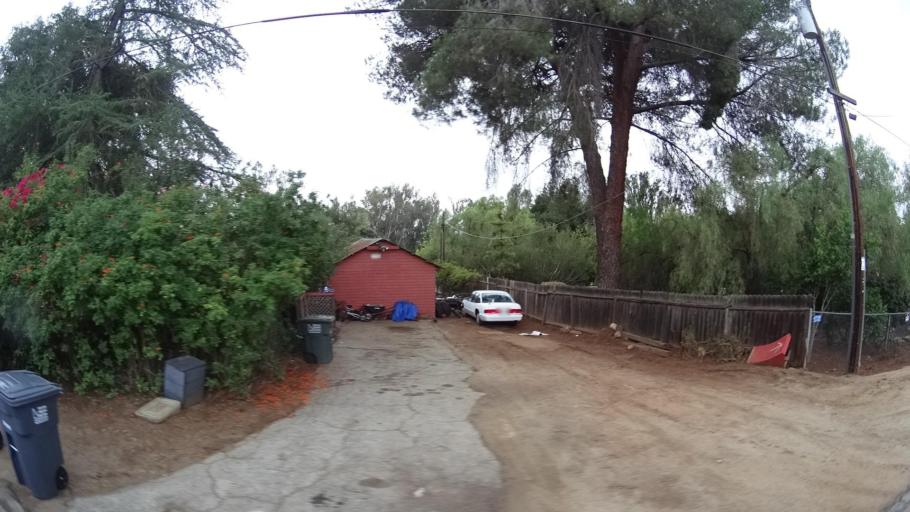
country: US
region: California
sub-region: San Diego County
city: Ramona
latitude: 33.0503
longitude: -116.8940
